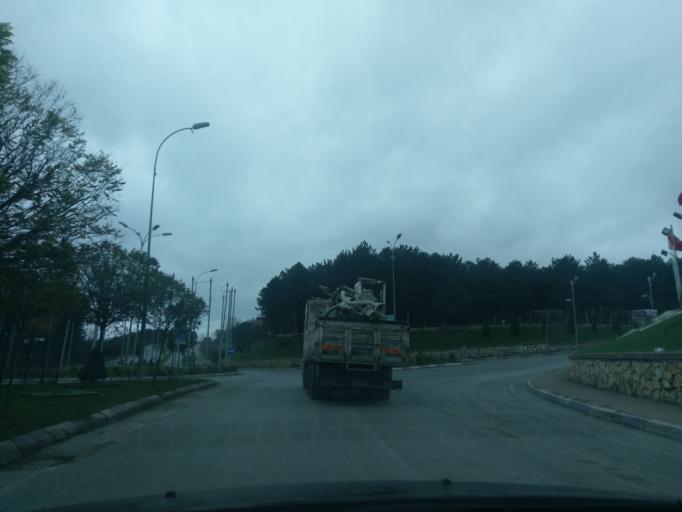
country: TR
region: Istanbul
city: Catalca
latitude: 41.1473
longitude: 28.4632
